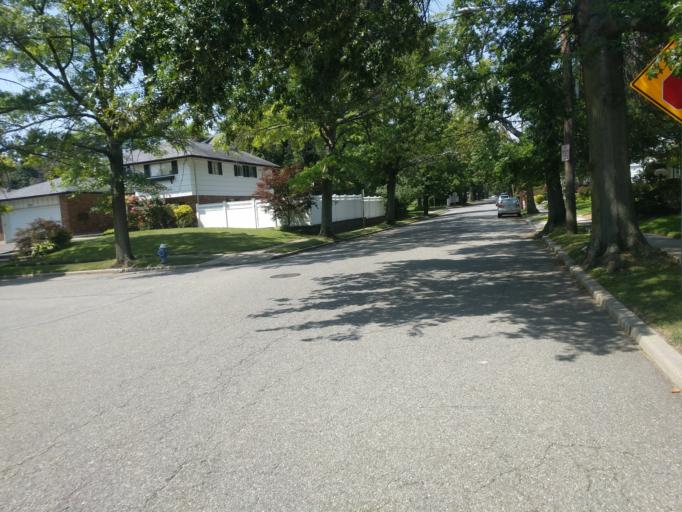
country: US
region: New York
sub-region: Nassau County
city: Woodmere
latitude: 40.6377
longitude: -73.7240
